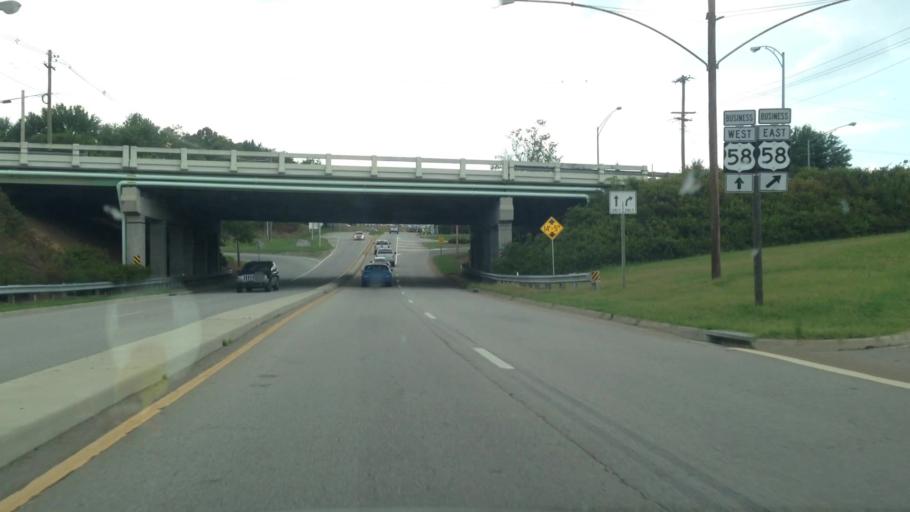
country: US
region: Virginia
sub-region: City of Danville
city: Danville
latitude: 36.5805
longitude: -79.4323
